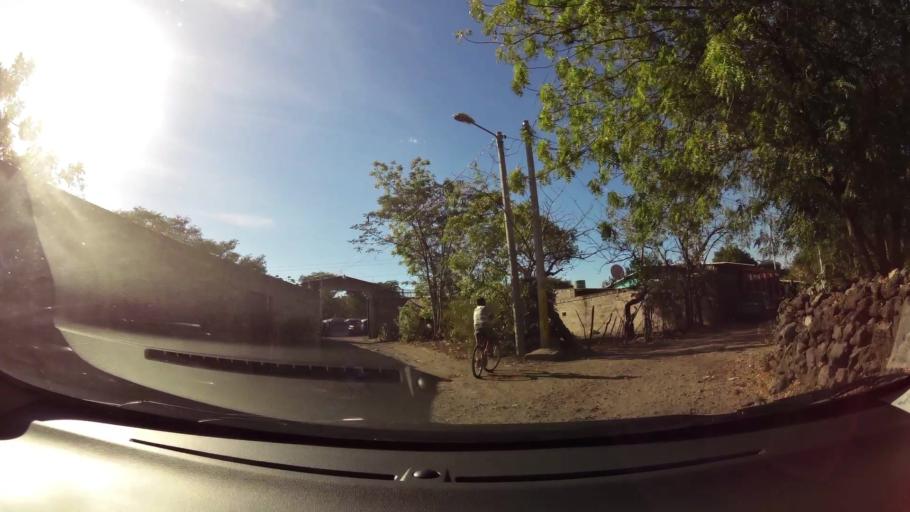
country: SV
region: San Miguel
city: San Miguel
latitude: 13.4652
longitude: -88.2009
